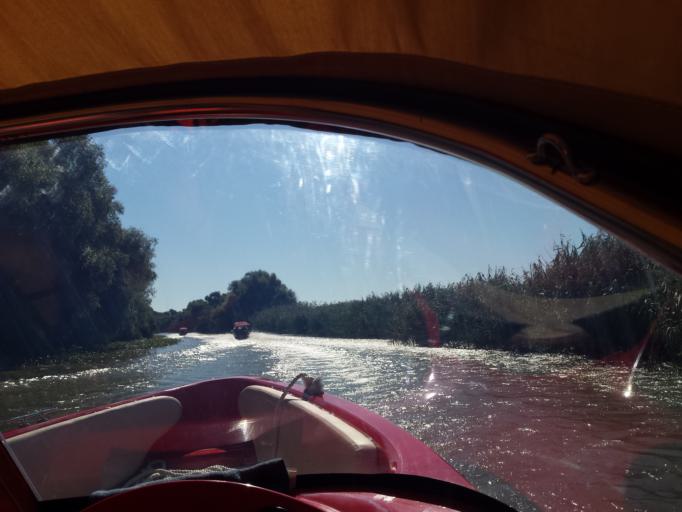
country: RO
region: Tulcea
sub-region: Comuna Pardina
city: Pardina
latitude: 45.2491
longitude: 29.0507
